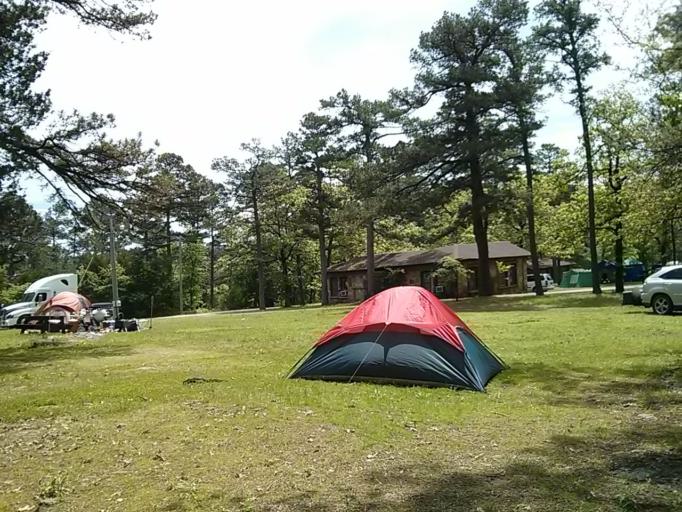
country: US
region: Oklahoma
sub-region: Latimer County
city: Wilburton
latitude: 35.0058
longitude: -95.3366
